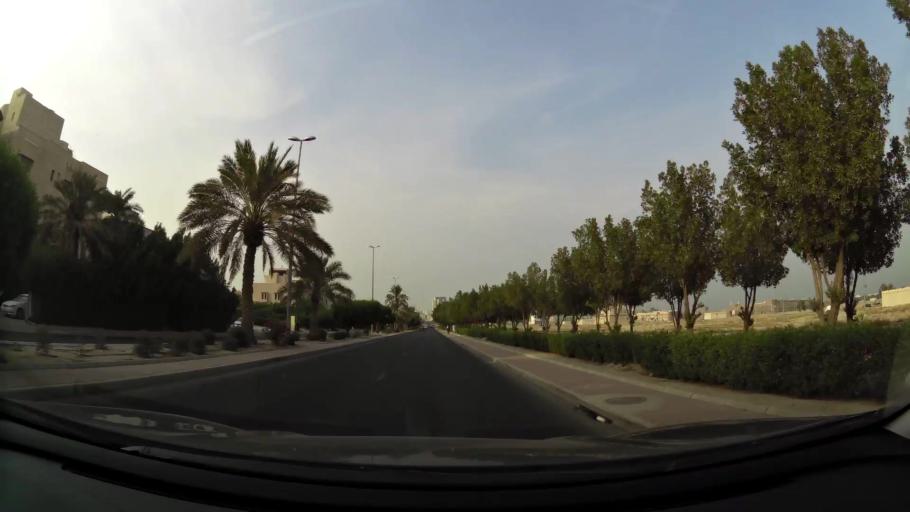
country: KW
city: Al Funaytis
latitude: 29.2379
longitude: 48.0837
